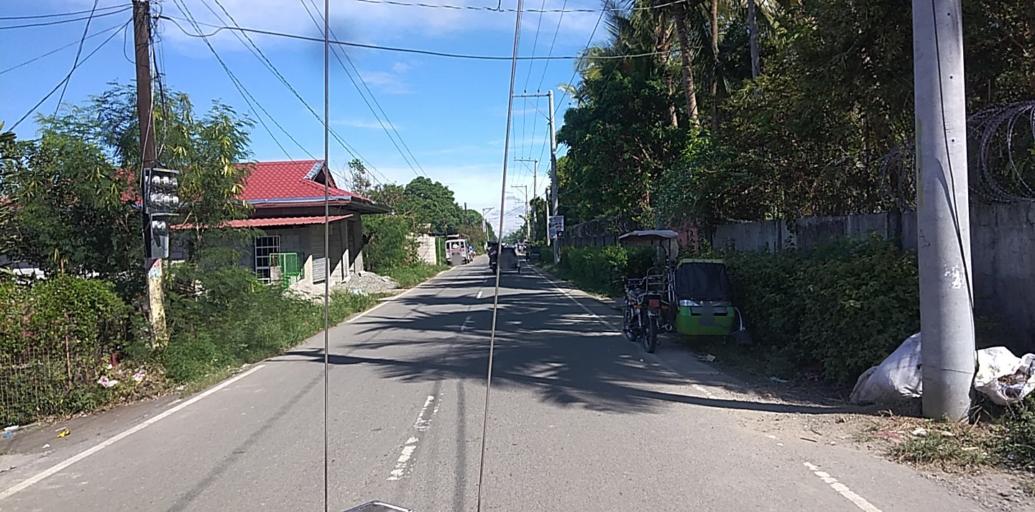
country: PH
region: Central Luzon
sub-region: Province of Pampanga
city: Candaba
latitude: 15.0906
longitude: 120.8115
